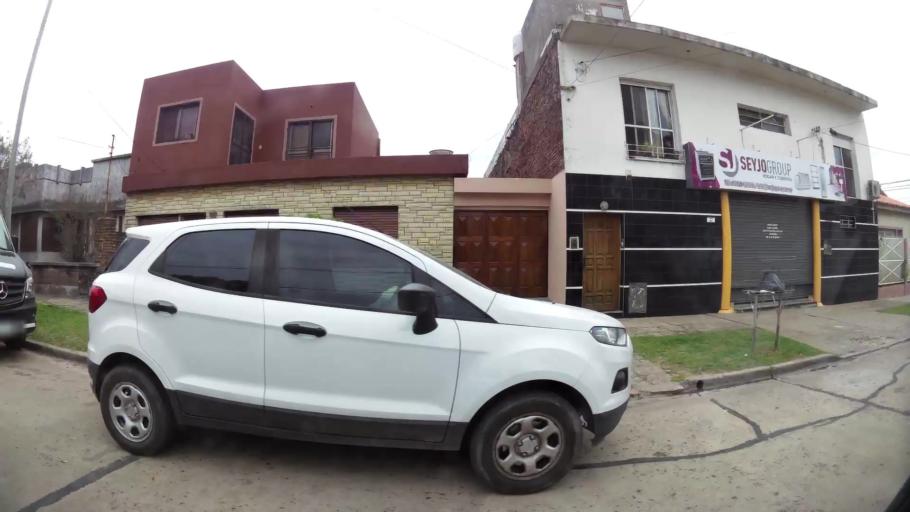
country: AR
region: Buenos Aires
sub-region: Partido de Campana
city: Campana
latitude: -34.1687
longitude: -58.9518
